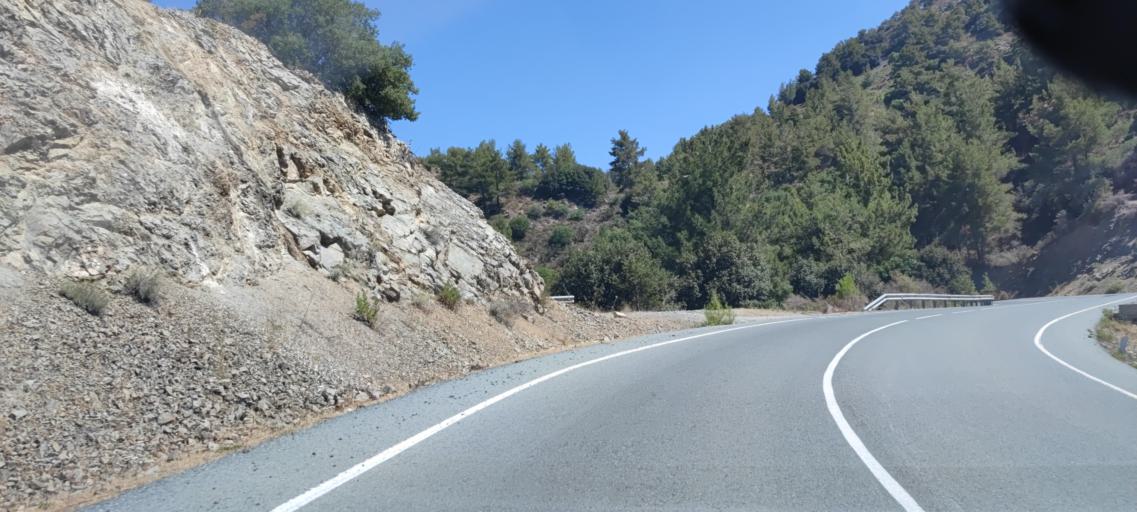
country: CY
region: Limassol
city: Pachna
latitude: 34.9011
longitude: 32.8148
